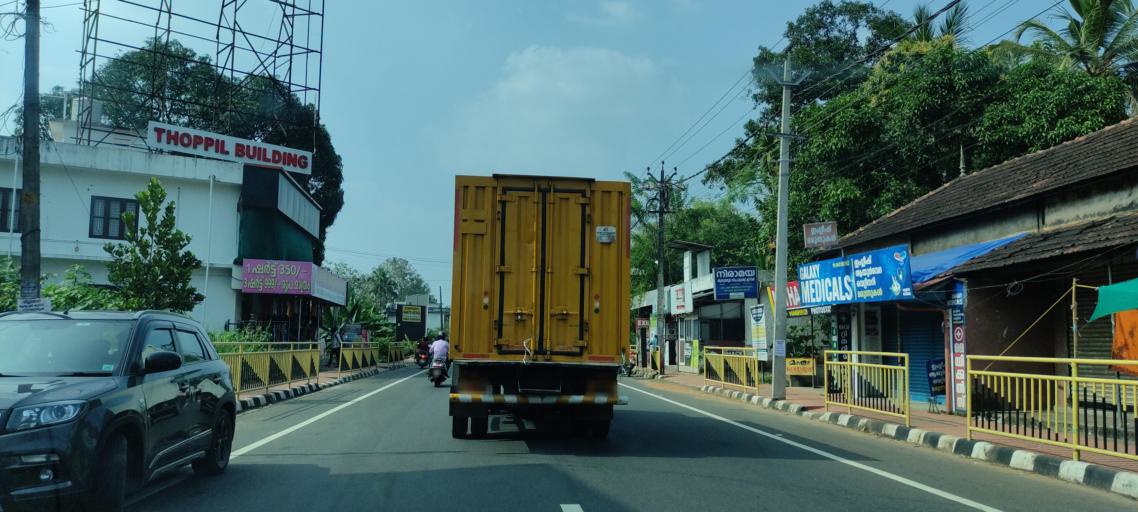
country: IN
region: Kerala
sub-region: Alappuzha
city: Chengannur
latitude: 9.2453
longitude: 76.6703
